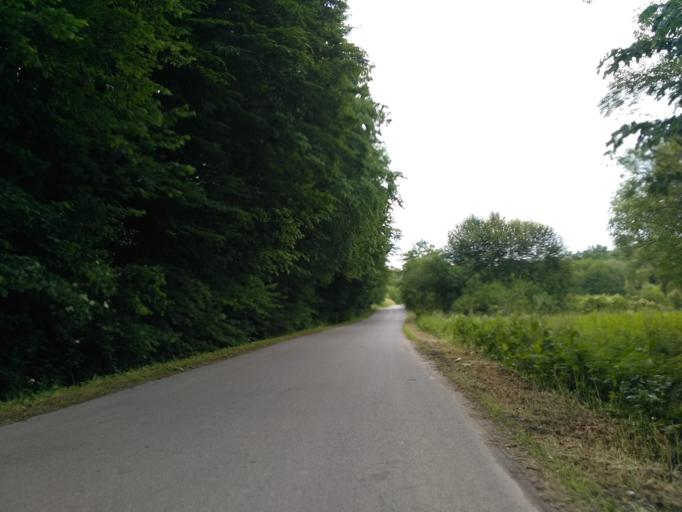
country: PL
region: Subcarpathian Voivodeship
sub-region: Powiat przeworski
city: Jawornik Polski
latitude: 49.8466
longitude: 22.3034
